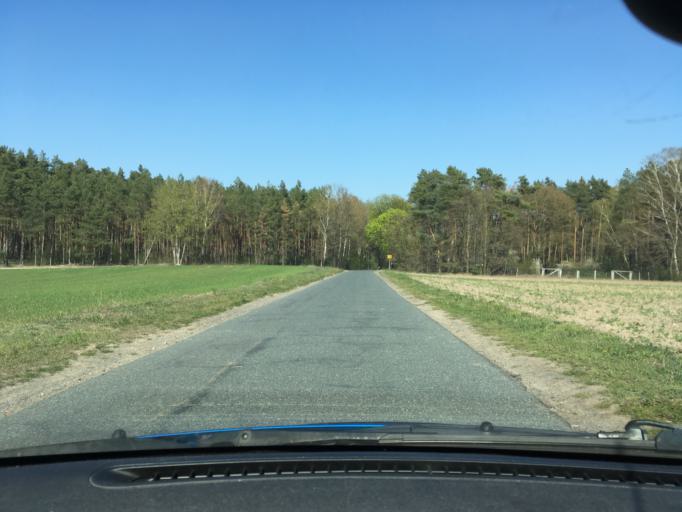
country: DE
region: Lower Saxony
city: Karwitz
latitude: 53.1224
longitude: 11.0098
